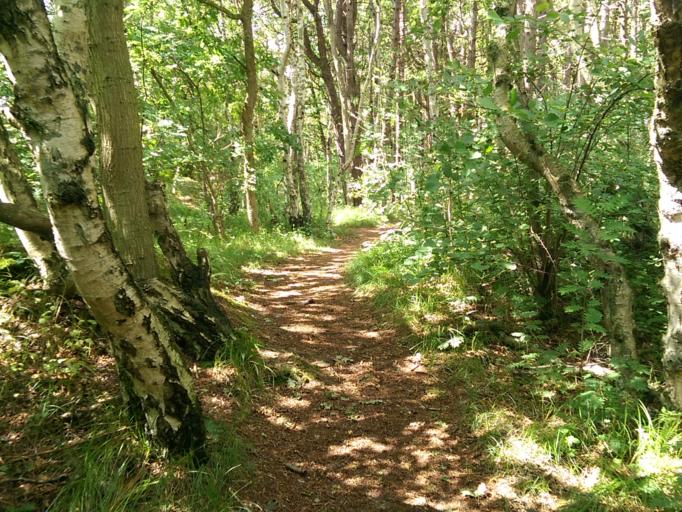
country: DE
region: Lower Saxony
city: Spiekeroog
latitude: 53.7728
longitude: 7.7060
